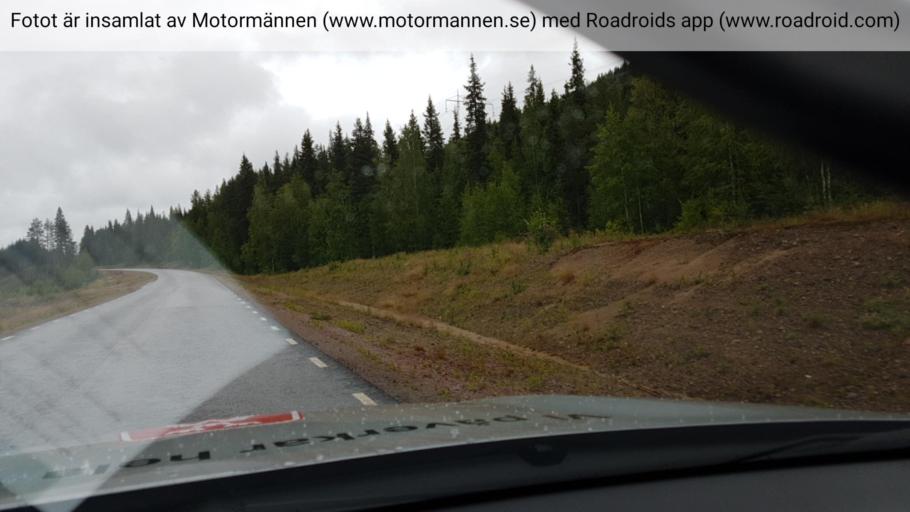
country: SE
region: Norrbotten
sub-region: Gallivare Kommun
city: Gaellivare
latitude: 66.6427
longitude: 20.3946
